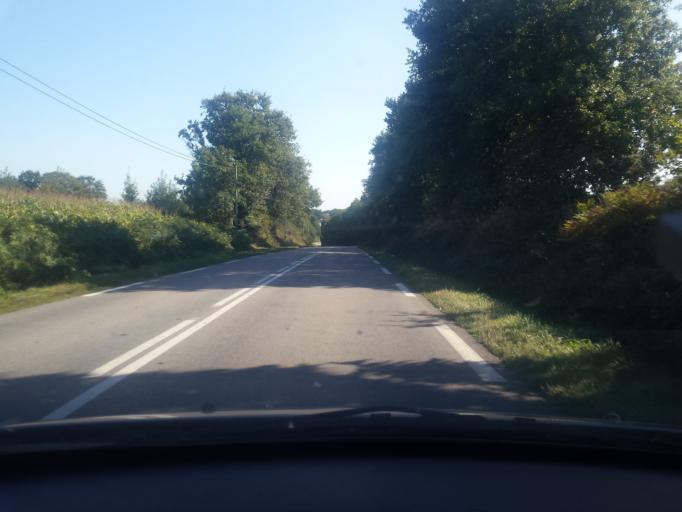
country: FR
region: Brittany
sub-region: Departement du Morbihan
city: Saint-Thuriau
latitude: 48.0440
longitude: -2.9259
